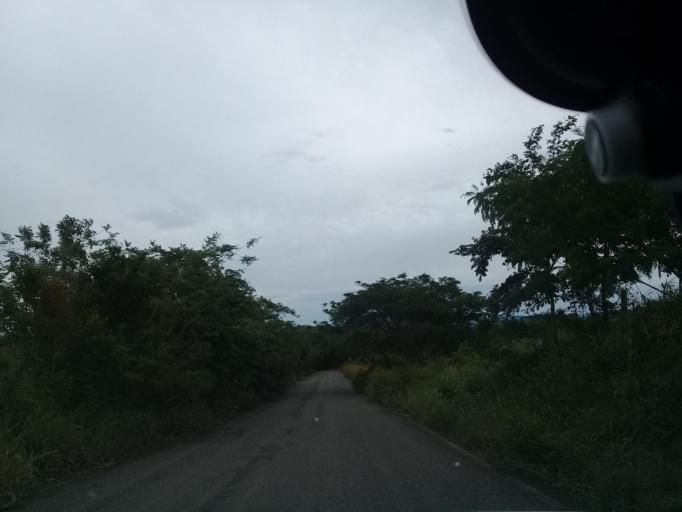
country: MX
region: Hidalgo
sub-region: Huejutla de Reyes
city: Chalahuiyapa
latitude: 21.2000
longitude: -98.3411
